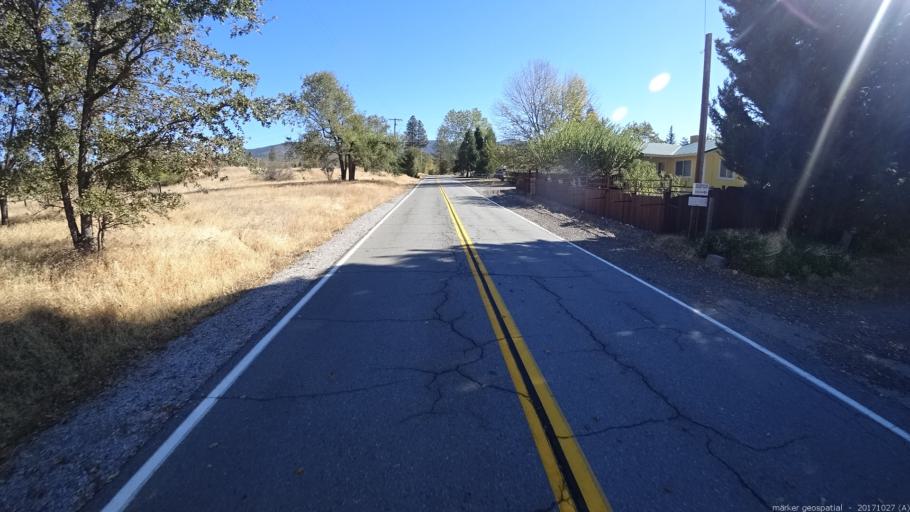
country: US
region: California
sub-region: Shasta County
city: Burney
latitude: 40.7942
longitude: -121.9391
